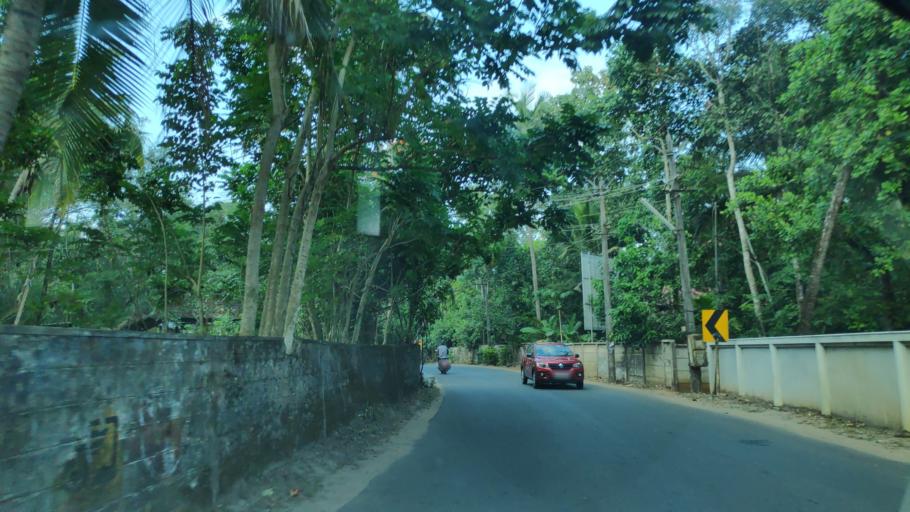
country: IN
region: Kerala
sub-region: Alappuzha
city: Shertallai
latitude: 9.6714
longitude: 76.3886
